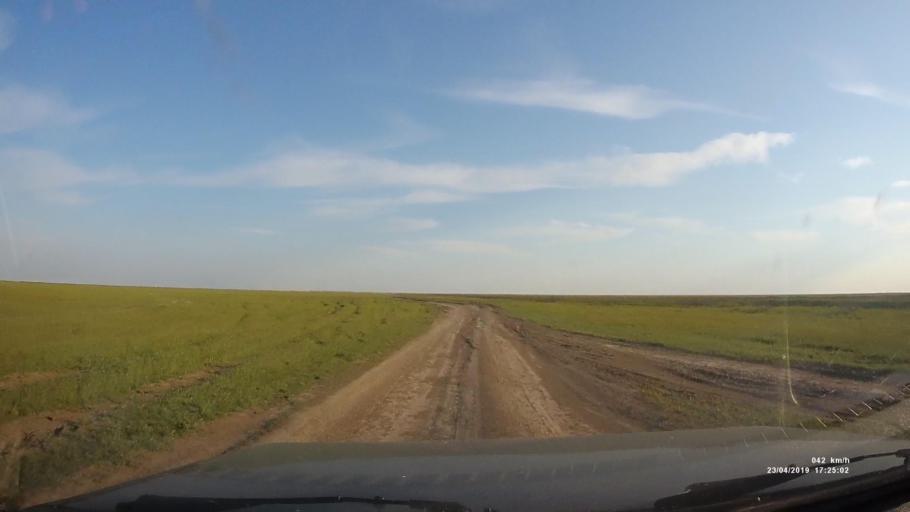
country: RU
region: Kalmykiya
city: Priyutnoye
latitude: 46.1542
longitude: 43.5097
